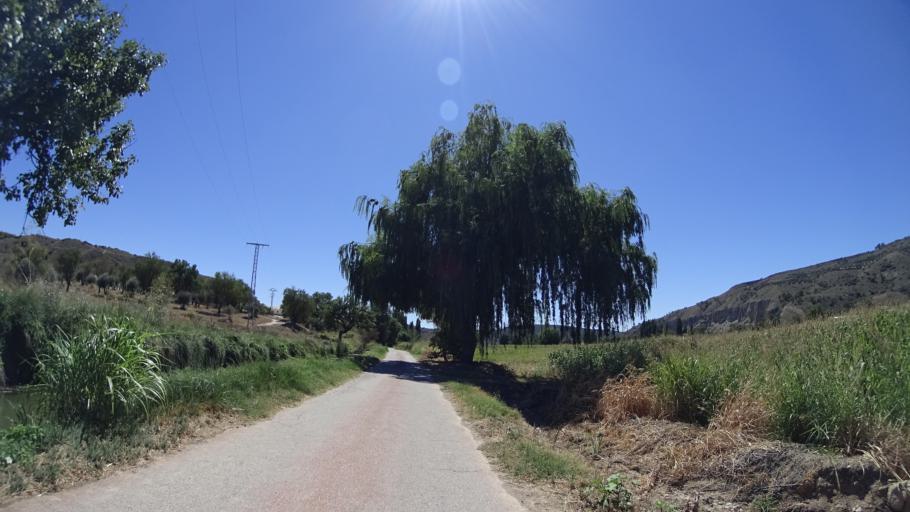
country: ES
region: Madrid
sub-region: Provincia de Madrid
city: Tielmes
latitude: 40.2335
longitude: -3.3225
